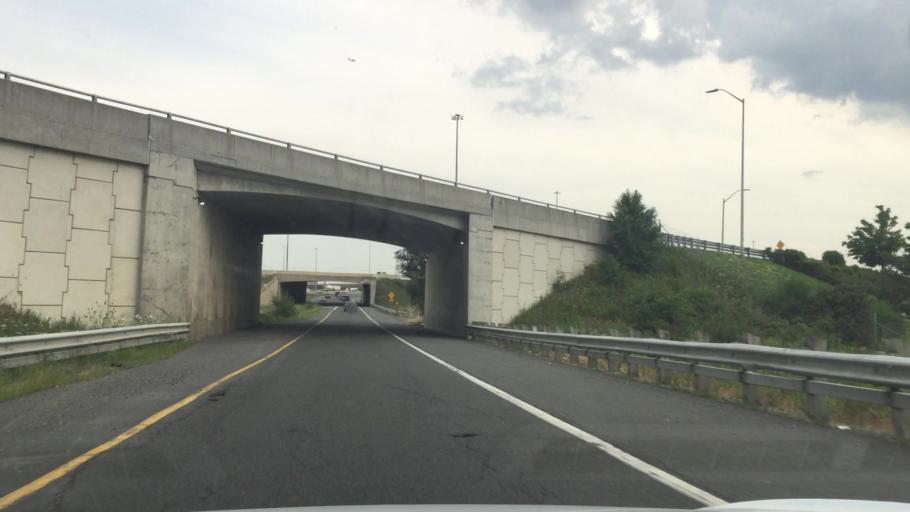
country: CA
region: Ontario
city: Concord
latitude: 43.7888
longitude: -79.5409
